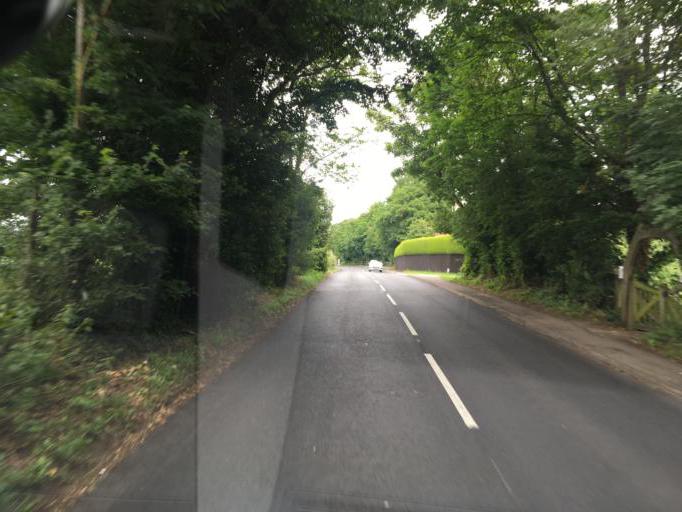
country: GB
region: England
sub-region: Gloucestershire
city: Stonehouse
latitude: 51.7517
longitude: -2.3163
